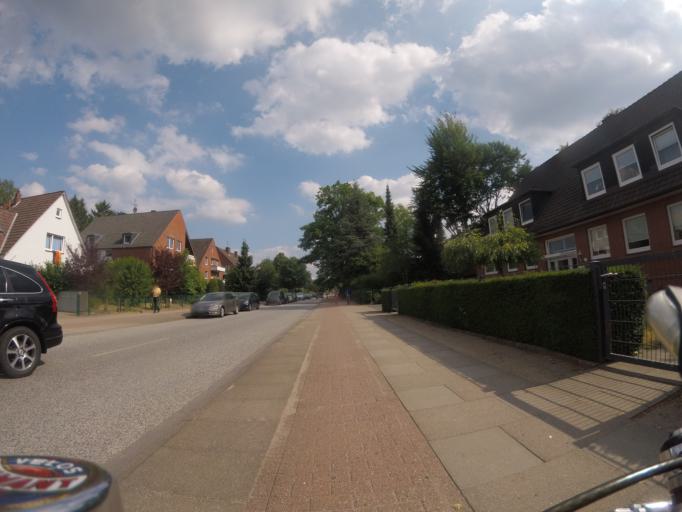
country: DE
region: Schleswig-Holstein
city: Bonningstedt
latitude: 53.6386
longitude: 9.9511
